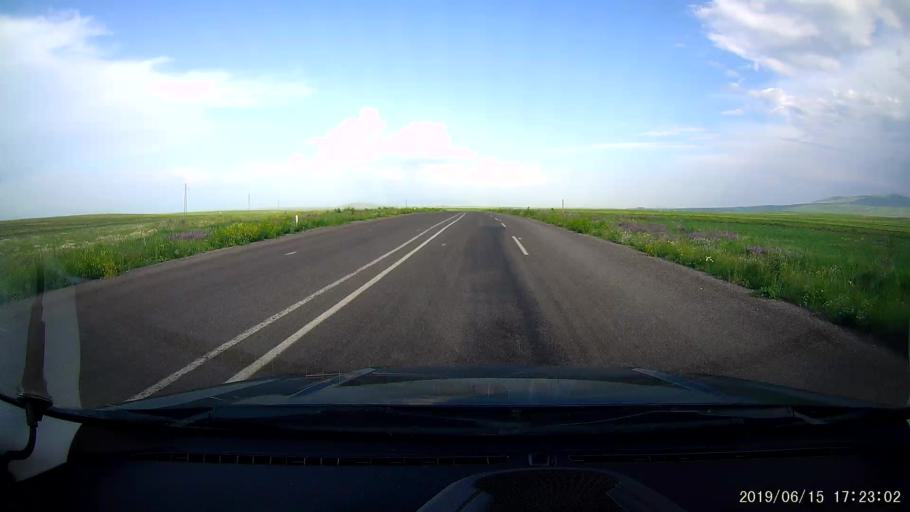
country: TR
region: Kars
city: Basgedikler
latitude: 40.6179
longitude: 43.3541
